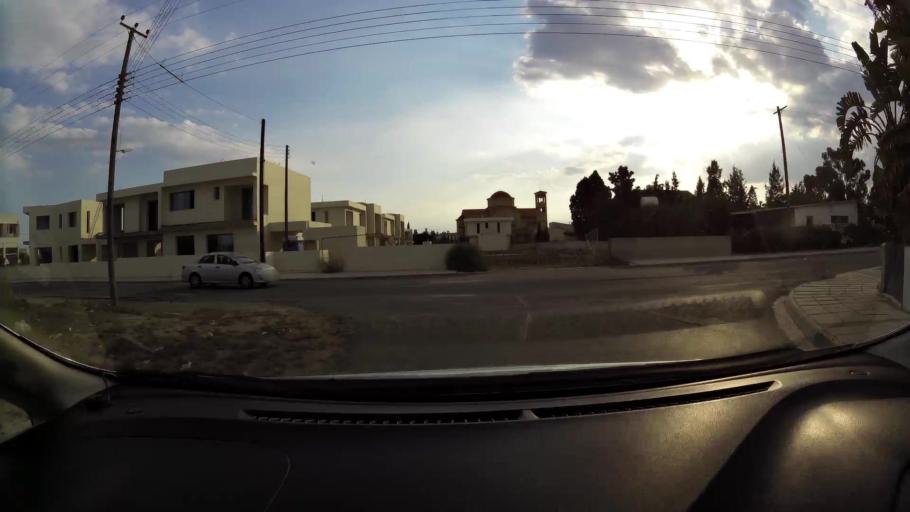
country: CY
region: Larnaka
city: Meneou
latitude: 34.8641
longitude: 33.5927
